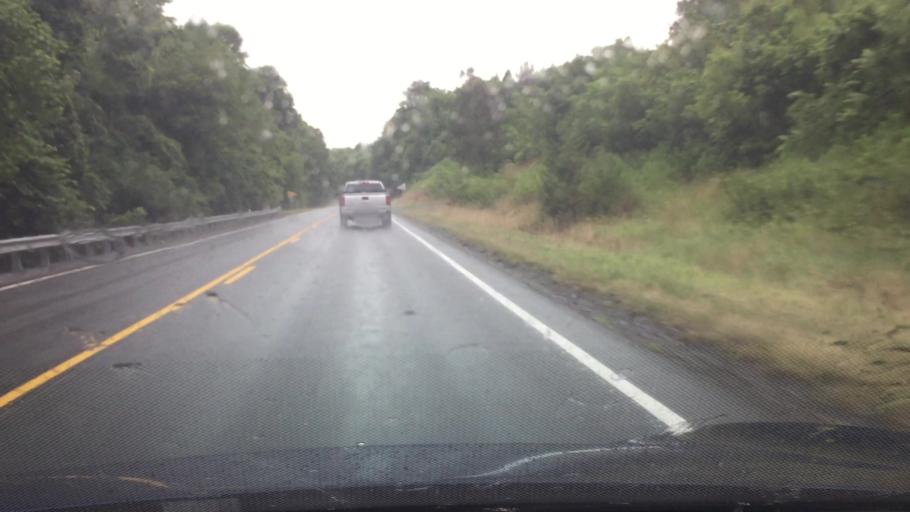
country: US
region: Virginia
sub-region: City of Bedford
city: Bedford
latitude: 37.3560
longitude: -79.4669
